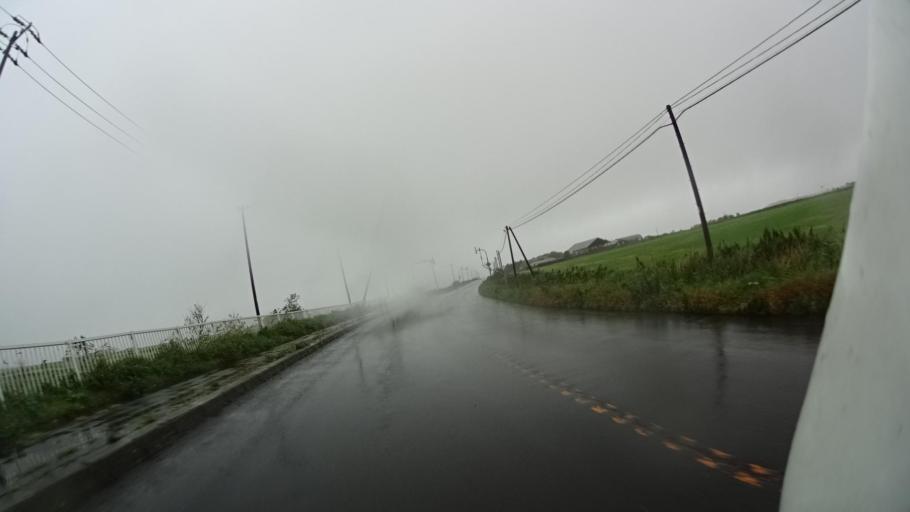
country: JP
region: Hokkaido
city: Nemuro
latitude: 43.2726
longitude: 145.5345
